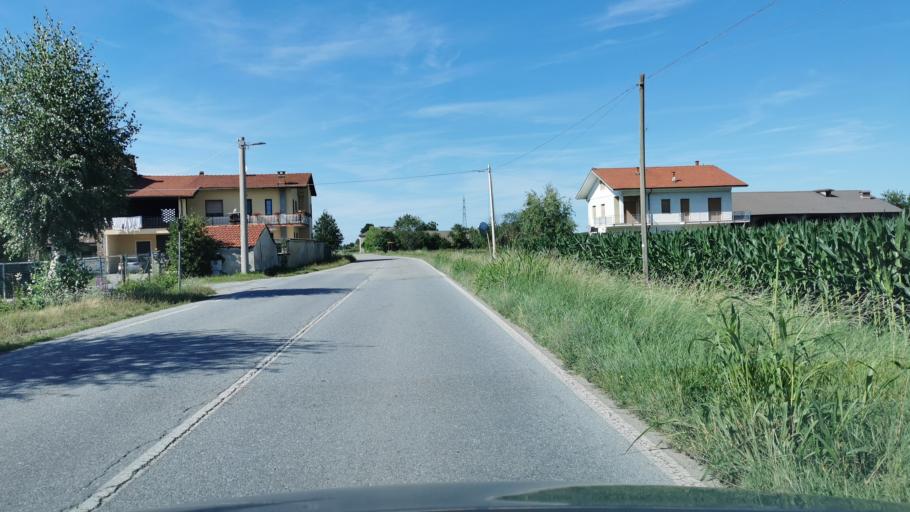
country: IT
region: Piedmont
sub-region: Provincia di Cuneo
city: Boves
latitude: 44.3475
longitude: 7.5582
